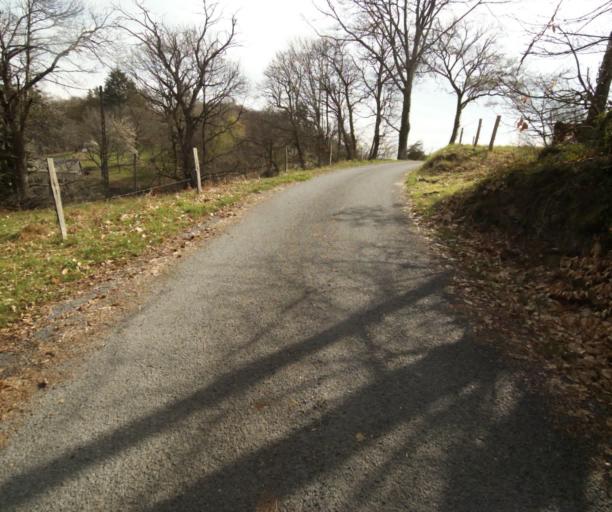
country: FR
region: Limousin
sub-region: Departement de la Correze
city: Correze
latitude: 45.3551
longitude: 1.8629
